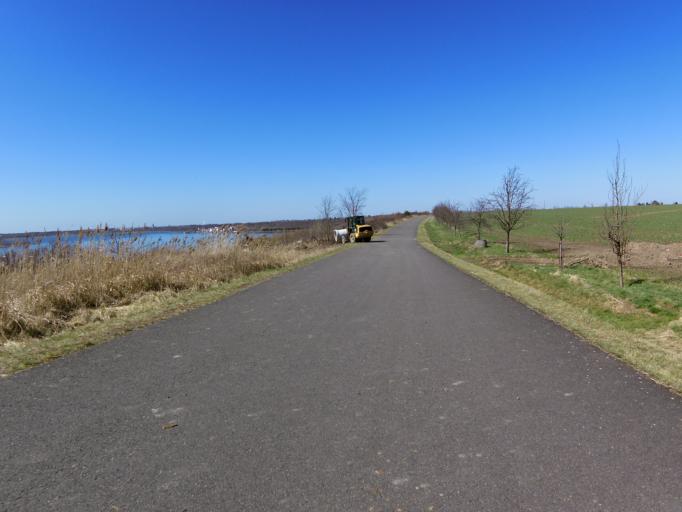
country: DE
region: Saxony
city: Markkleeberg
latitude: 51.2639
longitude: 12.4243
